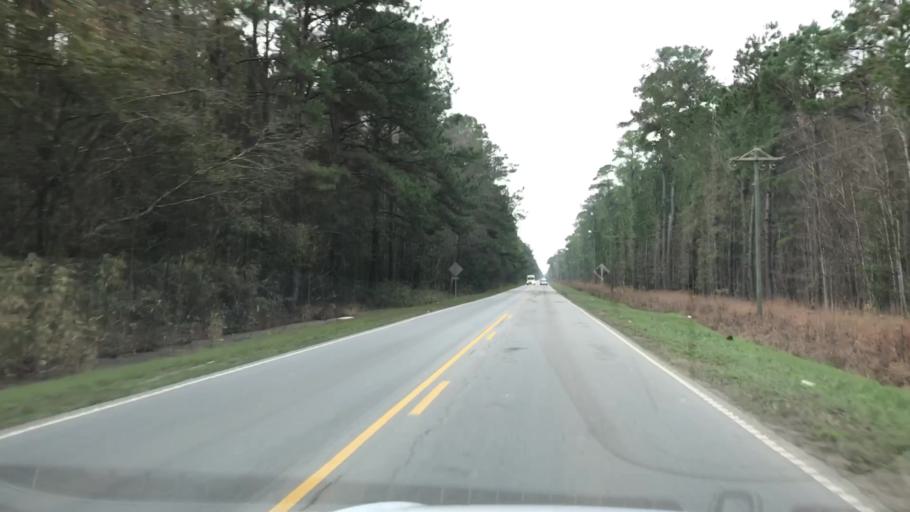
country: US
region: South Carolina
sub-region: Jasper County
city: Ridgeland
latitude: 32.3832
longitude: -80.9096
